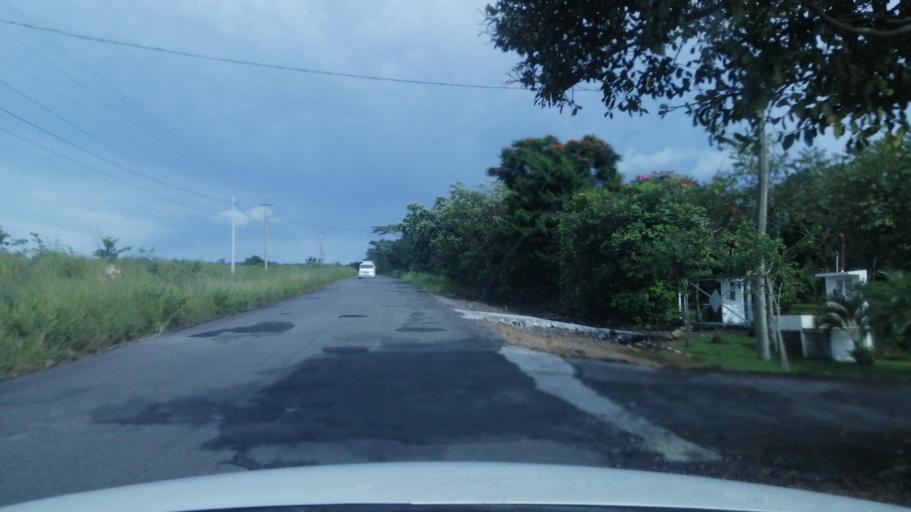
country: PA
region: Chiriqui
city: Potrerillos Abajo
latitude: 8.6707
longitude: -82.4346
